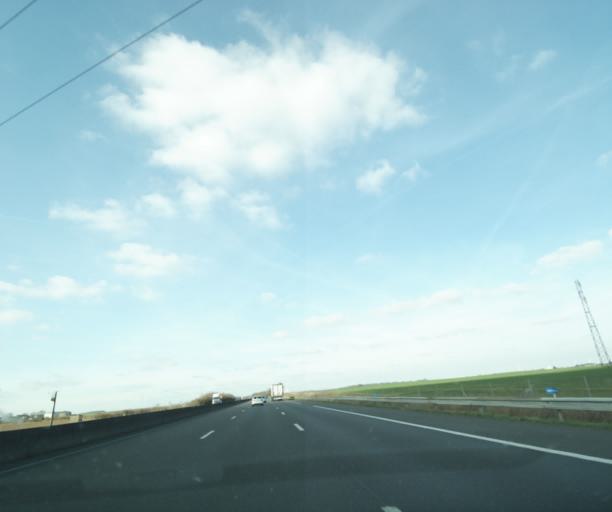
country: FR
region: Centre
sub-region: Departement d'Eure-et-Loir
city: Janville
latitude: 48.1815
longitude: 1.8543
